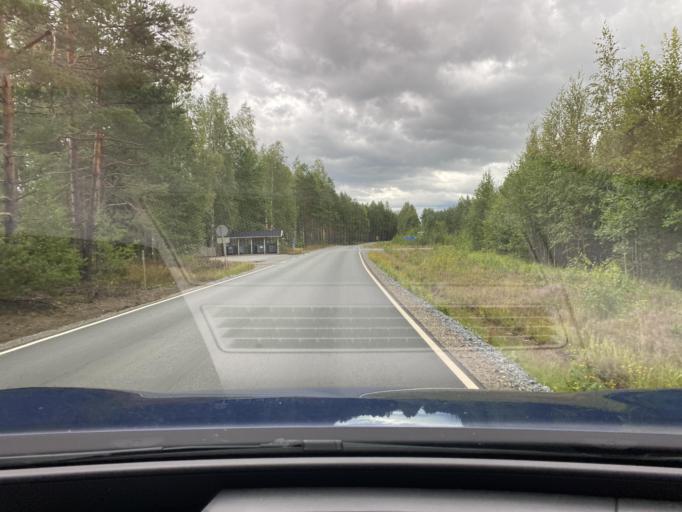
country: FI
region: Pirkanmaa
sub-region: Lounais-Pirkanmaa
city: Vammala
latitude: 61.2851
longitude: 23.0266
